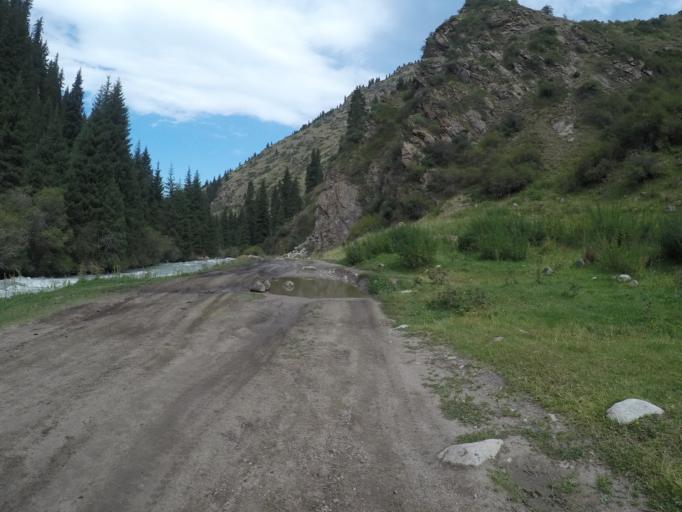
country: KG
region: Ysyk-Koel
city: Teploklyuchenka
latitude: 42.4399
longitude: 78.5576
